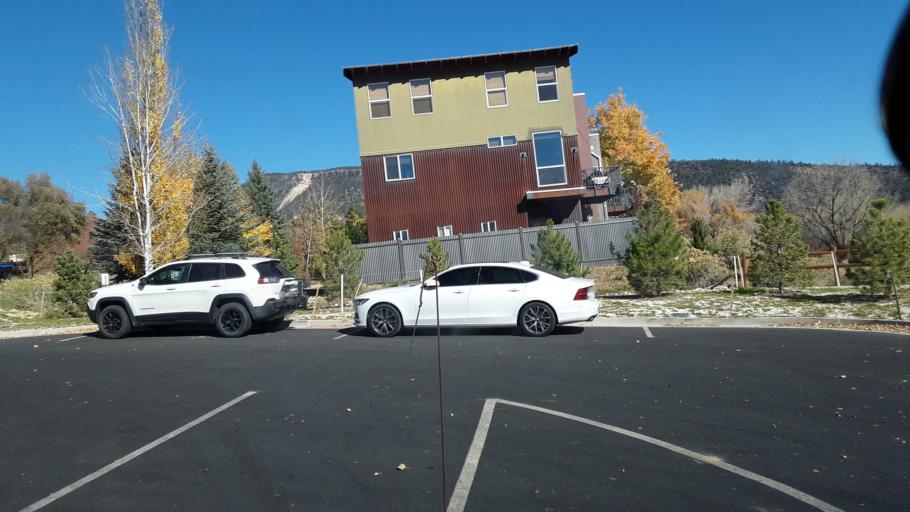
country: US
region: Colorado
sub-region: La Plata County
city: Durango
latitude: 37.3095
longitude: -107.8565
